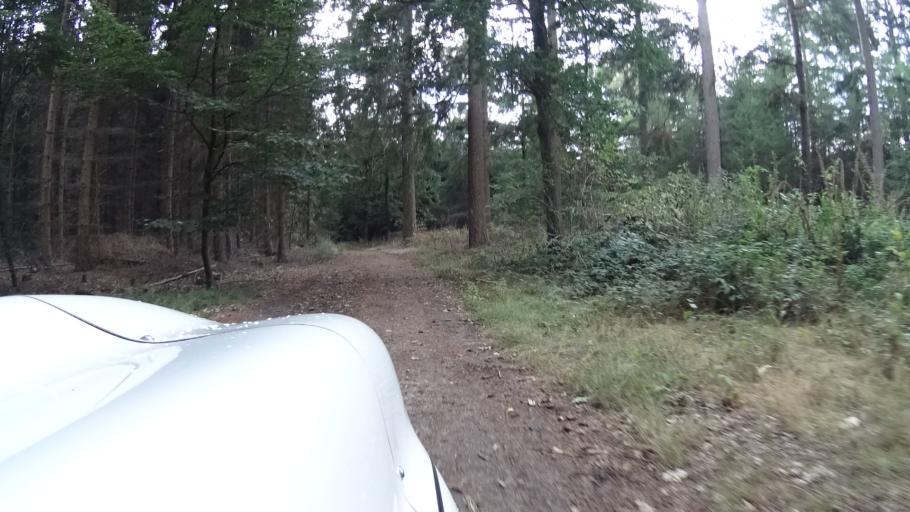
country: NL
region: Utrecht
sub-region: Gemeente Soest
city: Soest
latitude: 52.1847
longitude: 5.2526
